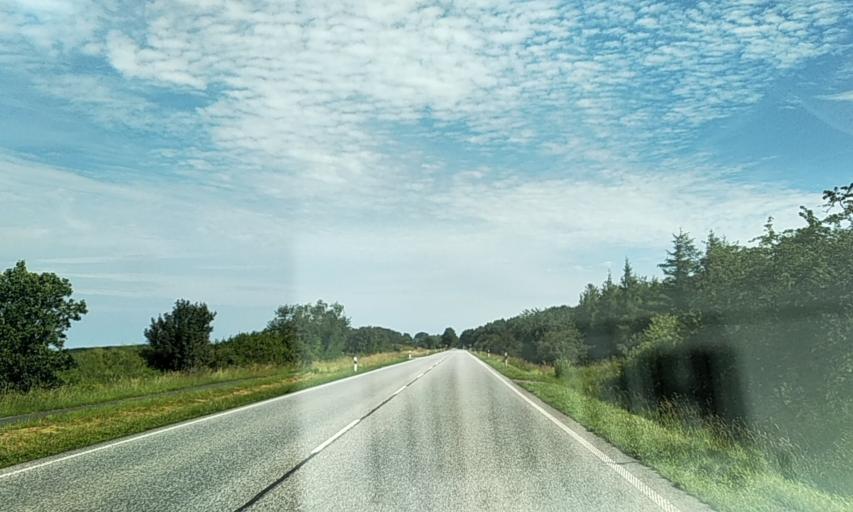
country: DE
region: Schleswig-Holstein
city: Jagel
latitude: 54.4480
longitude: 9.5374
